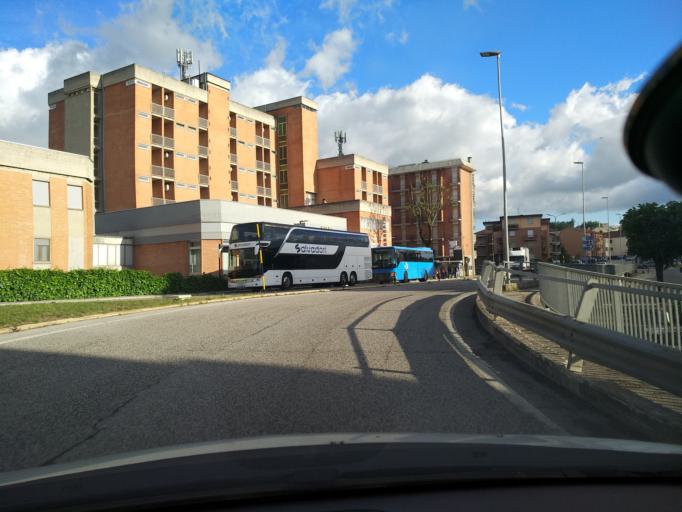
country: IT
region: The Marches
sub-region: Provincia di Pesaro e Urbino
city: Urbino
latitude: 43.7334
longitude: 12.6321
